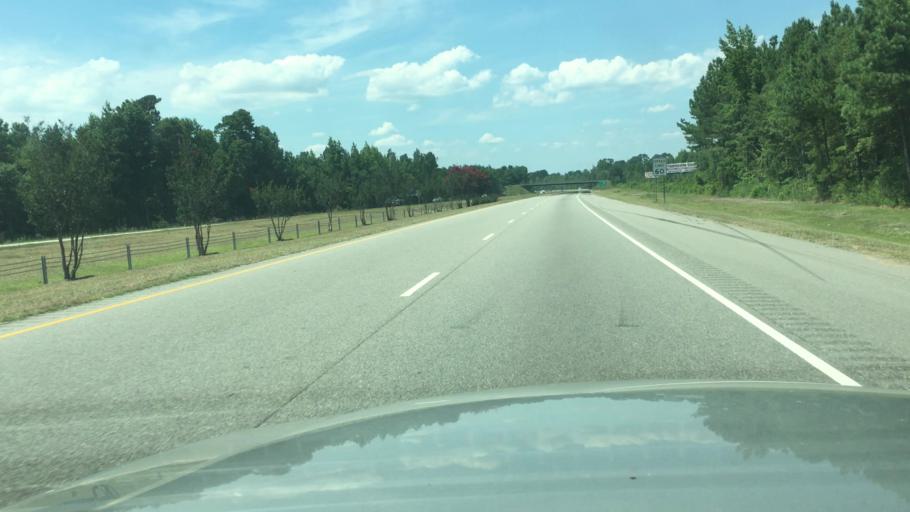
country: US
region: North Carolina
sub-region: Cumberland County
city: Fayetteville
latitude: 35.0181
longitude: -78.8711
